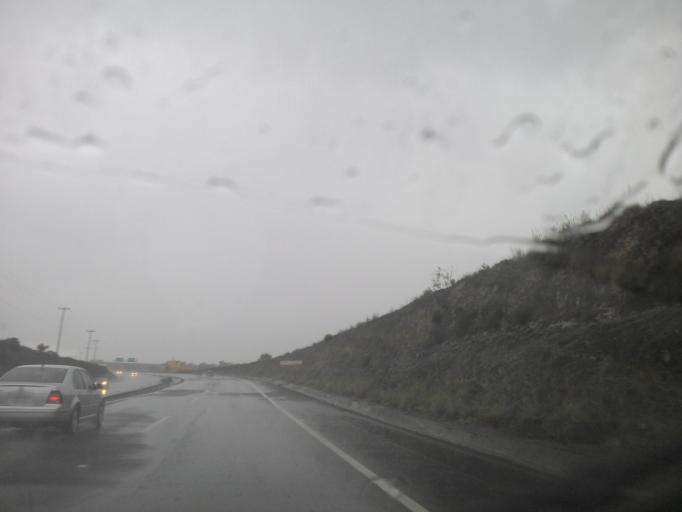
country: MX
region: Morelos
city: Nopaltepec
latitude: 19.8443
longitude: -98.6880
